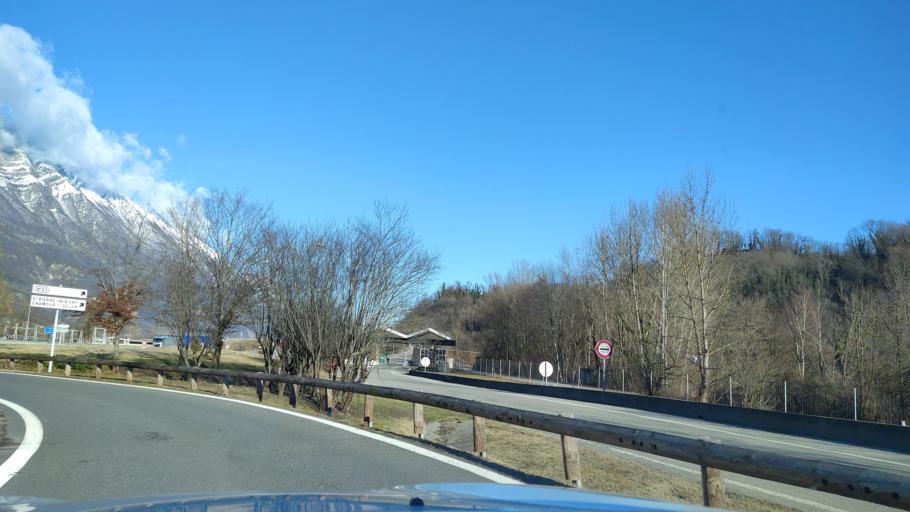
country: FR
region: Rhone-Alpes
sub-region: Departement de la Savoie
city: Coise-Saint-Jean-Pied-Gauthier
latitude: 45.5477
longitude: 6.1587
